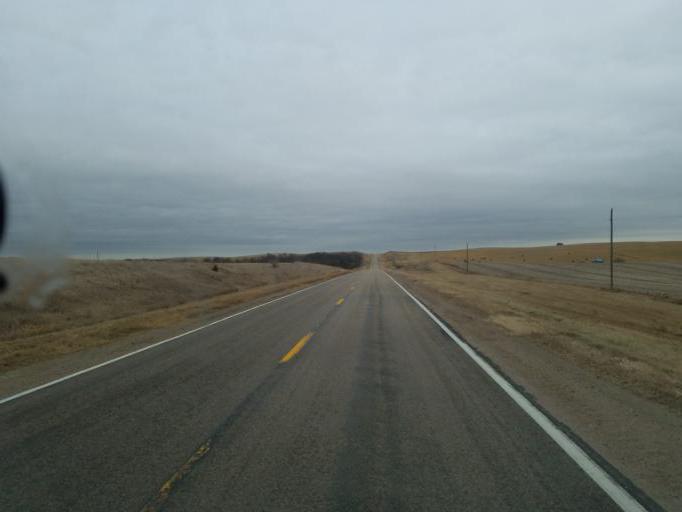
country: US
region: Nebraska
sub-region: Knox County
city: Bloomfield
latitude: 42.6127
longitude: -97.4993
